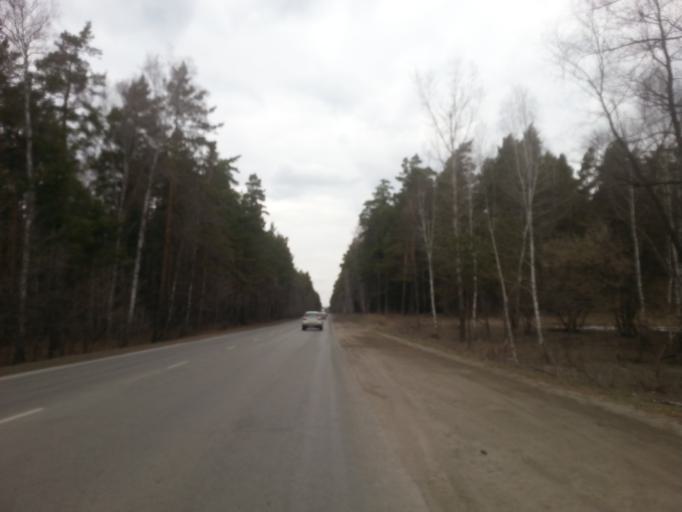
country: RU
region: Altai Krai
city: Yuzhnyy
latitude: 53.2769
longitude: 83.7197
